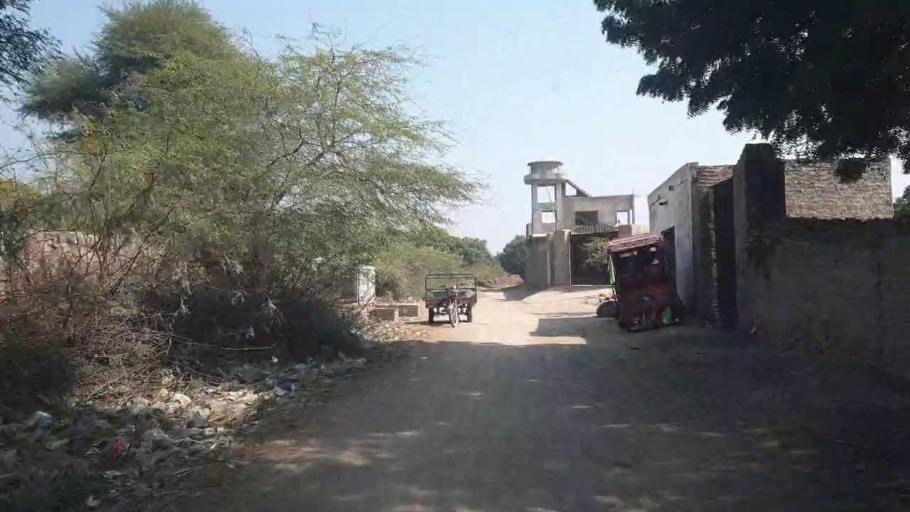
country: PK
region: Sindh
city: Tando Allahyar
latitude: 25.4800
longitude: 68.8467
